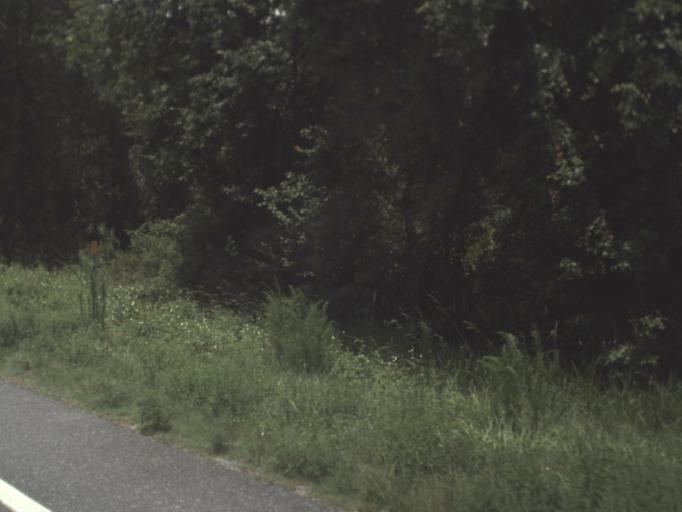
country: US
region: Florida
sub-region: Gilchrist County
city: Trenton
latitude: 29.6235
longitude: -82.7491
